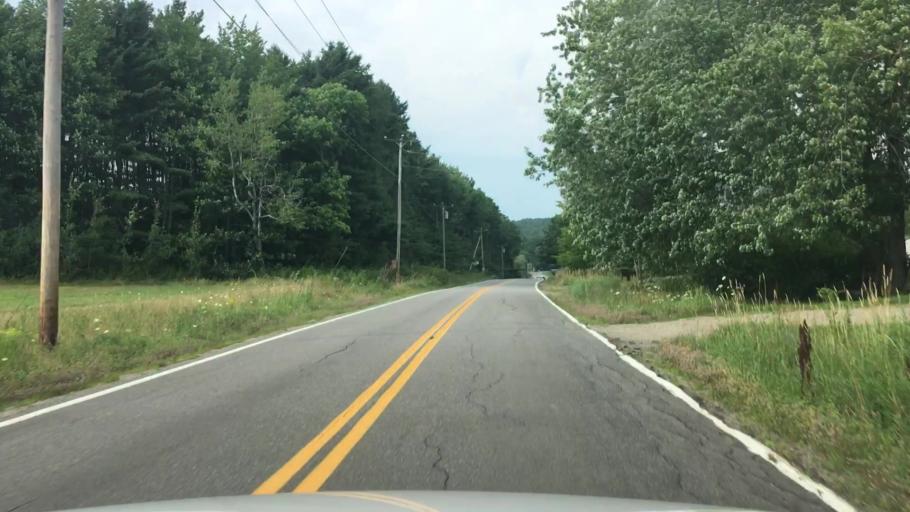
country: US
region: Maine
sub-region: Knox County
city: Washington
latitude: 44.2844
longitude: -69.3663
